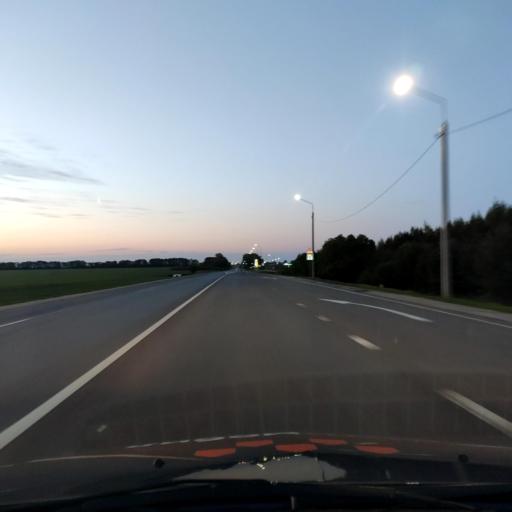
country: RU
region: Orjol
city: Zmiyevka
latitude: 52.7133
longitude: 36.3477
